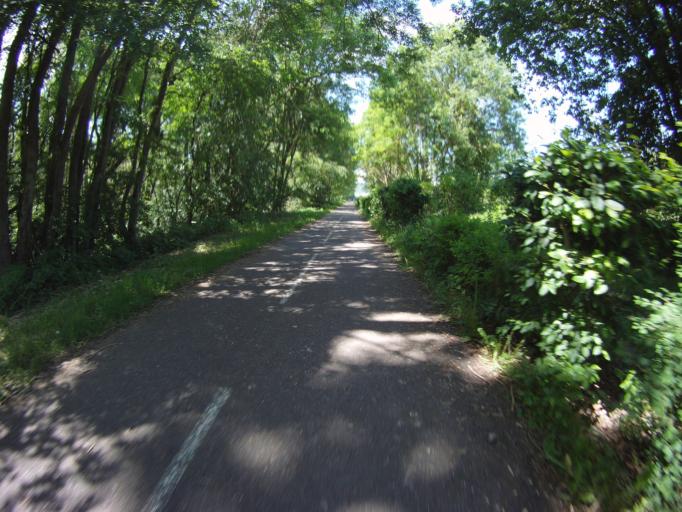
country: FR
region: Lorraine
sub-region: Departement de Meurthe-et-Moselle
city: Eulmont
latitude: 48.7436
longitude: 6.2147
